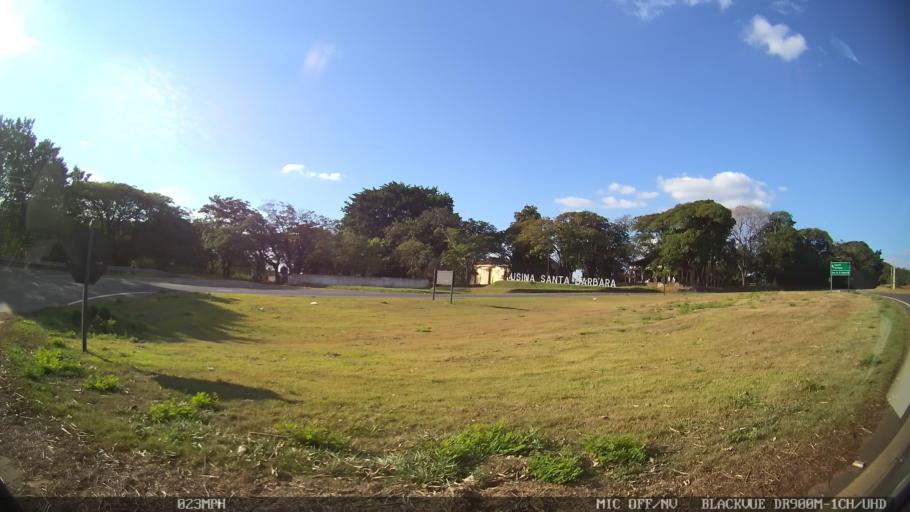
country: BR
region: Sao Paulo
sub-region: Santa Barbara D'Oeste
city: Santa Barbara d'Oeste
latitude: -22.7573
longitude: -47.4419
